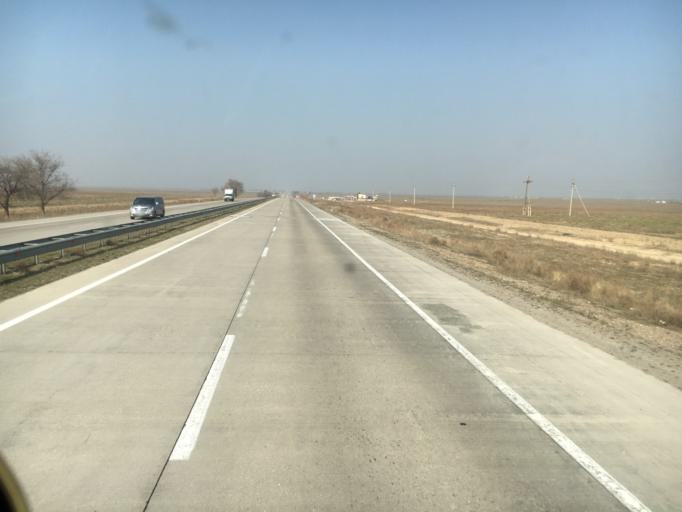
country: KZ
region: Ongtustik Qazaqstan
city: Temirlanovka
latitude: 42.8358
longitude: 69.1168
